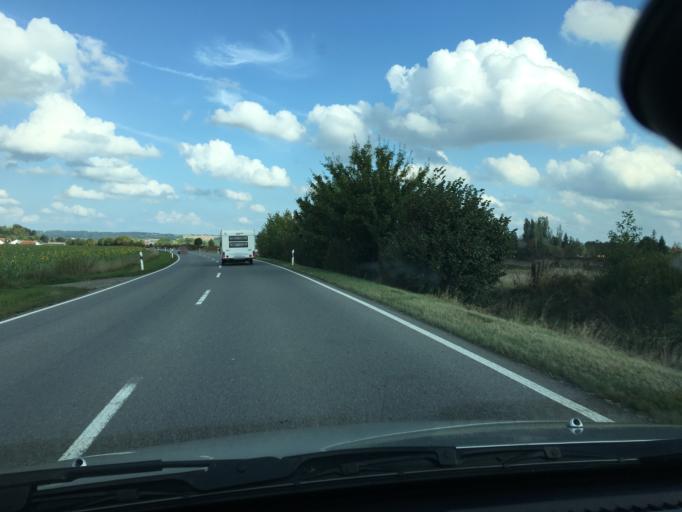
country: DE
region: Baden-Wuerttemberg
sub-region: Tuebingen Region
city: Ingoldingen
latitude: 48.0237
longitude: 9.7226
